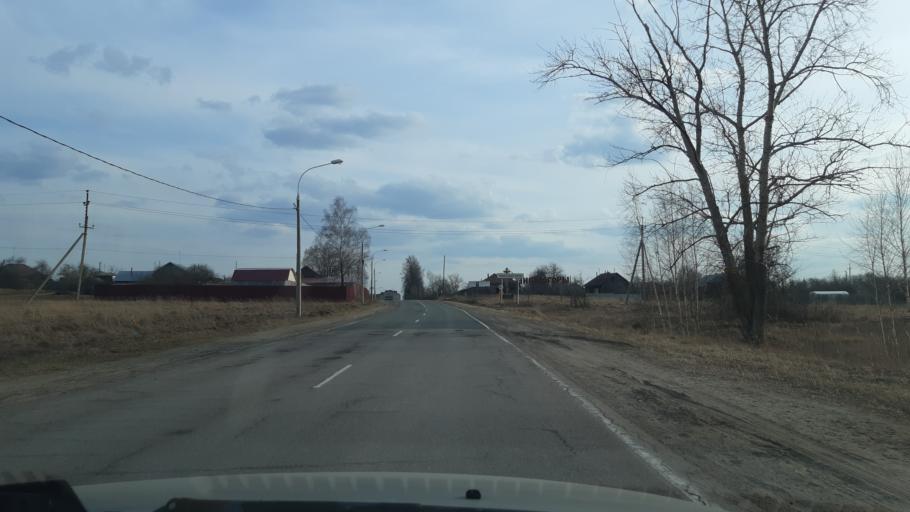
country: RU
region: Vladimir
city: Nikologory
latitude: 56.1529
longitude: 41.9956
